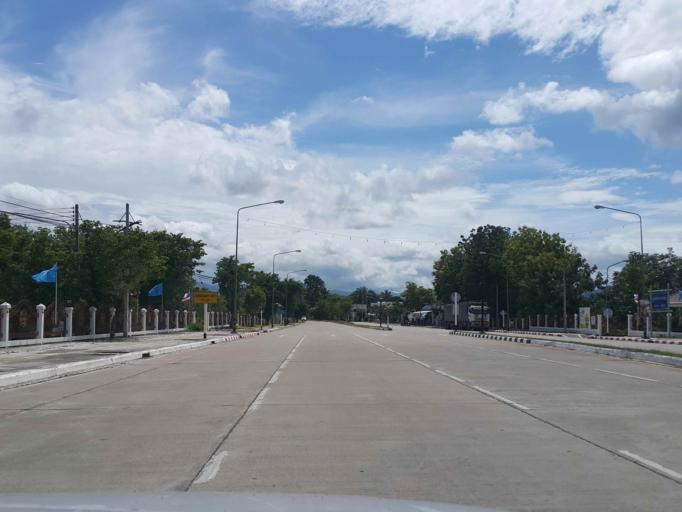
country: TH
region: Tak
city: Tak
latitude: 16.8815
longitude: 99.1133
